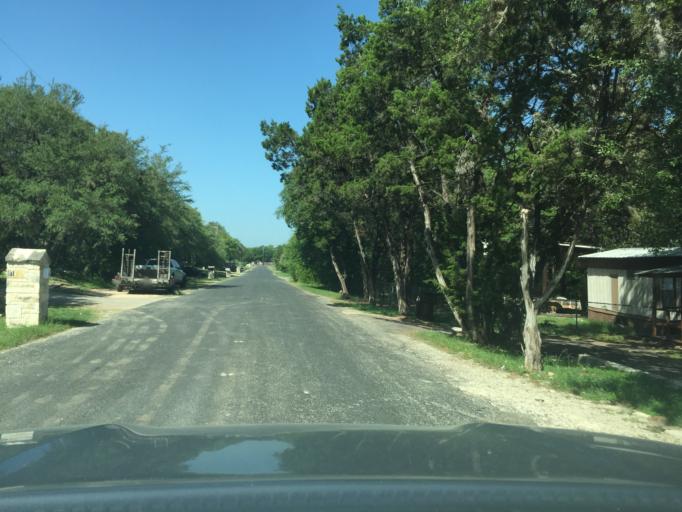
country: US
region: Texas
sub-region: Bexar County
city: Timberwood Park
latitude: 29.7057
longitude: -98.4762
